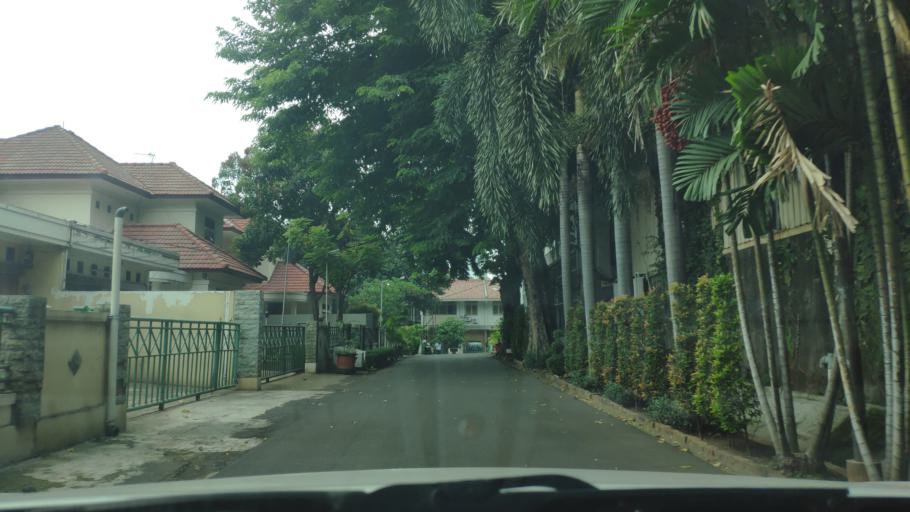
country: ID
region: Jakarta Raya
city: Jakarta
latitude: -6.1918
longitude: 106.7964
